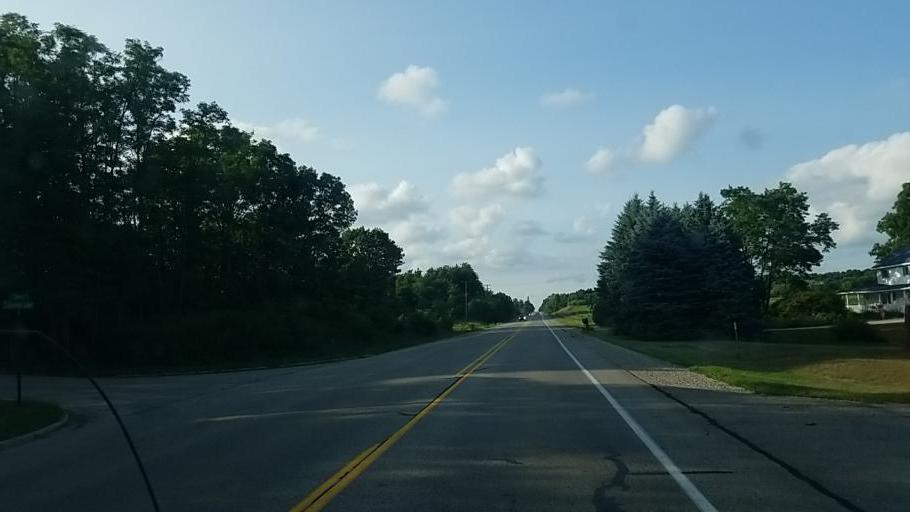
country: US
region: Michigan
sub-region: Kent County
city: Lowell
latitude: 42.9945
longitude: -85.3518
